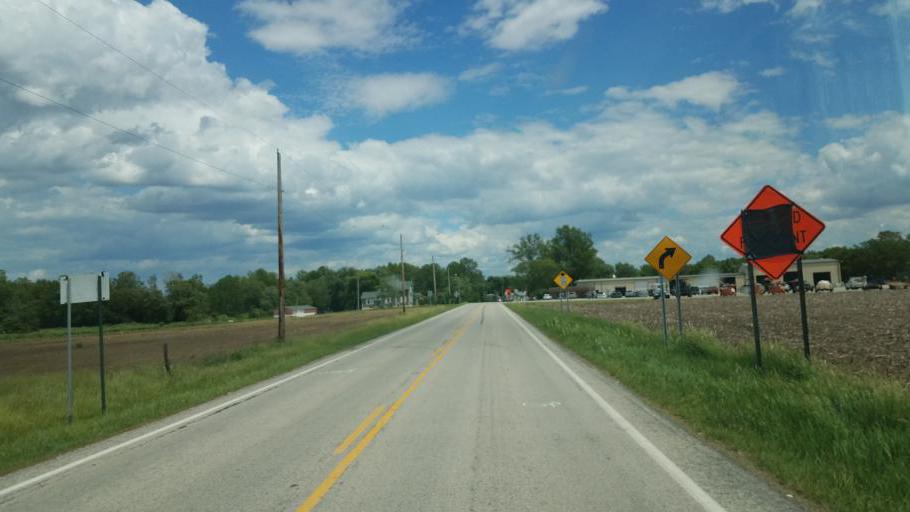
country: US
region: Ohio
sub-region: Huron County
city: Monroeville
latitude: 41.2408
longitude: -82.7168
